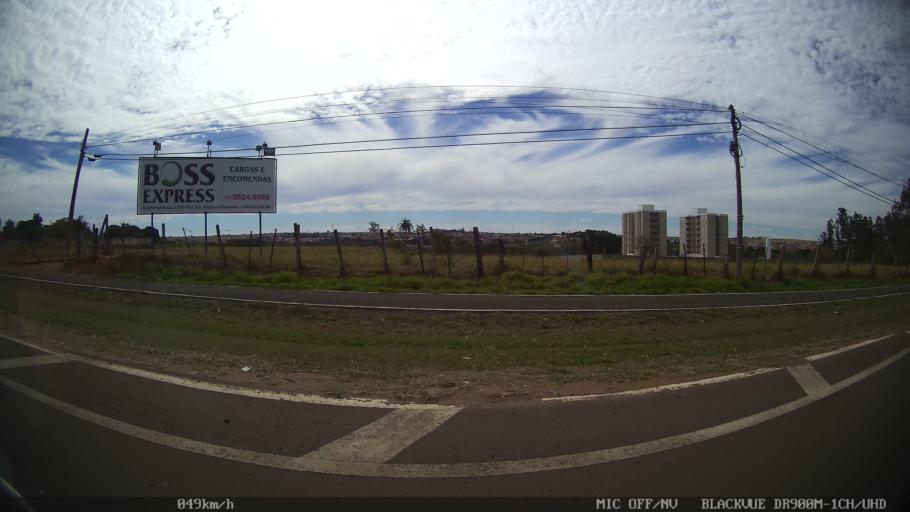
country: BR
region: Sao Paulo
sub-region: Catanduva
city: Catanduva
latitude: -21.1527
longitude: -48.9568
